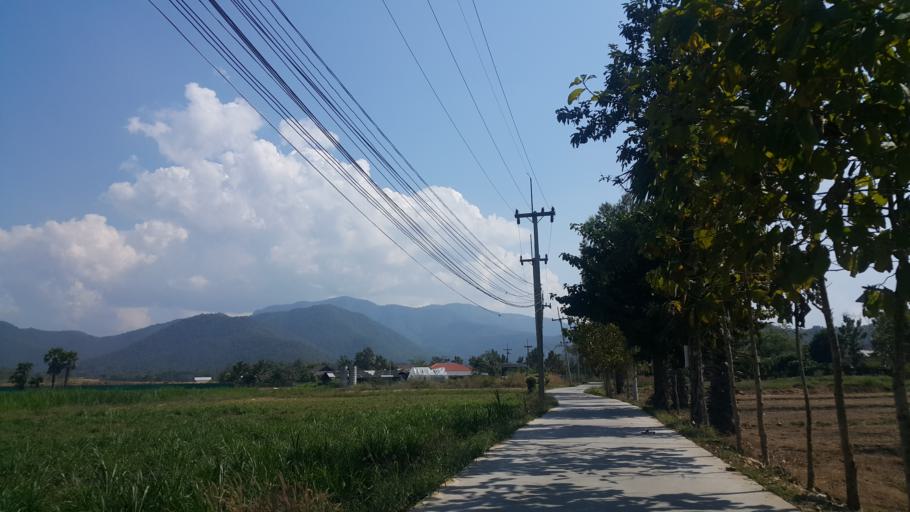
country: TH
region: Lamphun
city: Ban Thi
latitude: 18.6838
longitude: 99.1583
